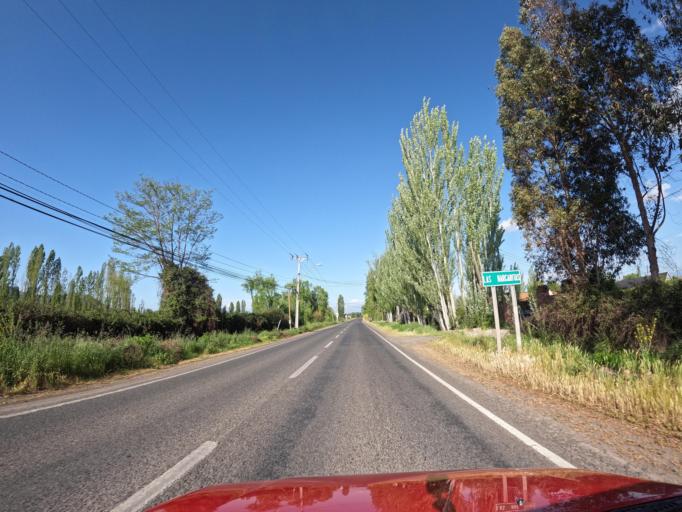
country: CL
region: Maule
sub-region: Provincia de Curico
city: Teno
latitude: -34.8685
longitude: -71.2329
